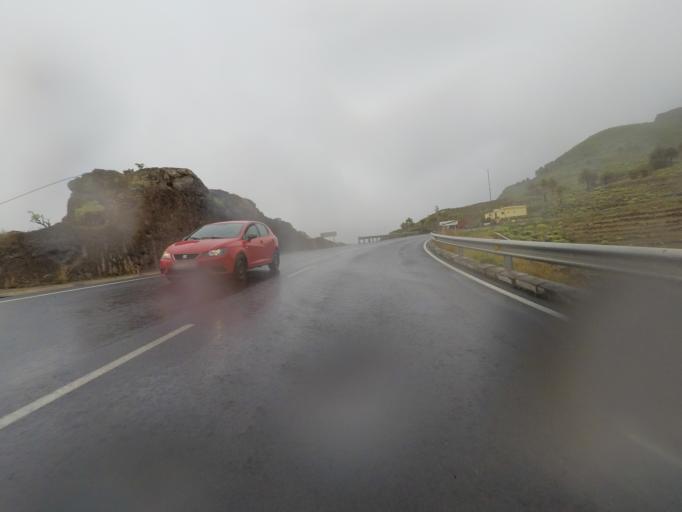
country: ES
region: Canary Islands
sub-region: Provincia de Santa Cruz de Tenerife
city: Alajero
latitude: 28.0763
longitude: -17.2088
